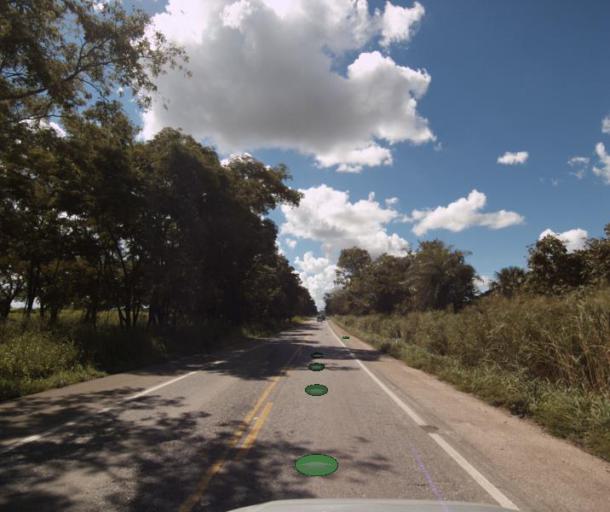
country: BR
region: Goias
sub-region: Porangatu
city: Porangatu
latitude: -13.6497
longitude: -49.0390
